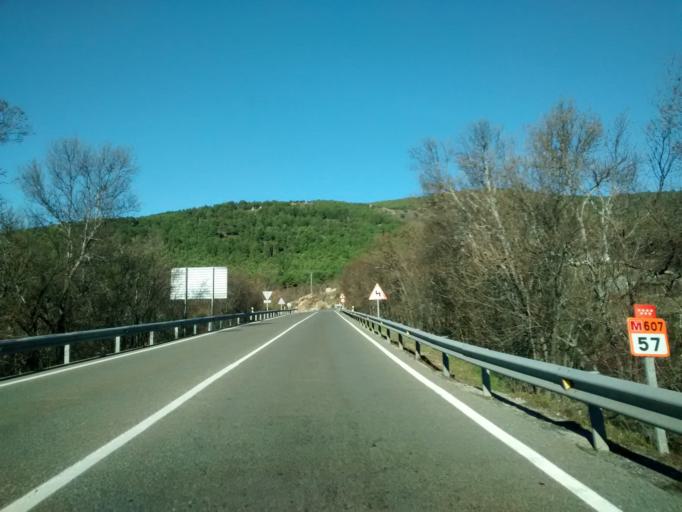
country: ES
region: Madrid
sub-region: Provincia de Madrid
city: Navacerrada
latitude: 40.7343
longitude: -4.0075
